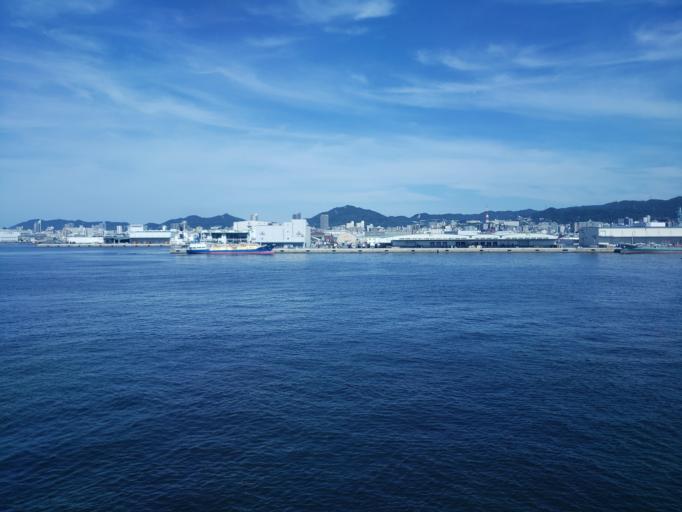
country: JP
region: Hyogo
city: Kobe
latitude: 34.6635
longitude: 135.1907
